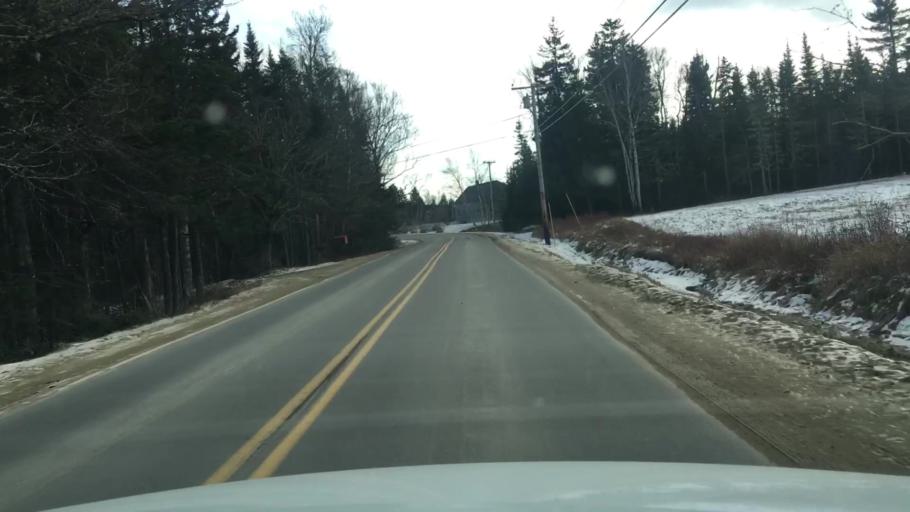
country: US
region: Maine
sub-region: Washington County
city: Jonesport
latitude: 44.6108
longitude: -67.6020
